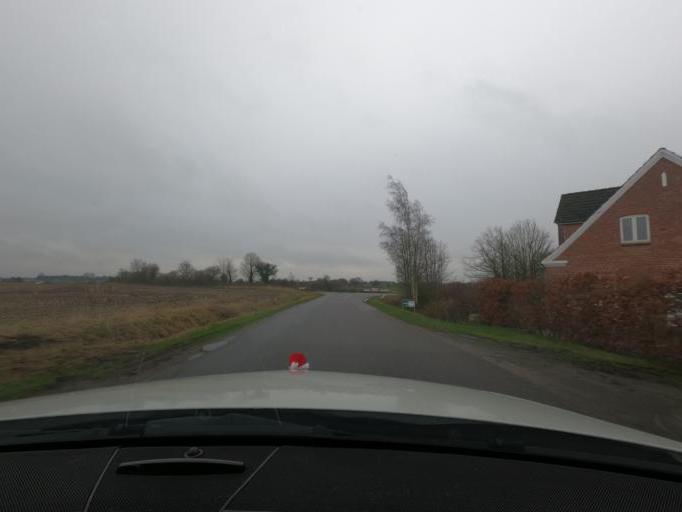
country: DK
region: South Denmark
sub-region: Haderslev Kommune
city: Haderslev
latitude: 55.1927
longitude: 9.4911
